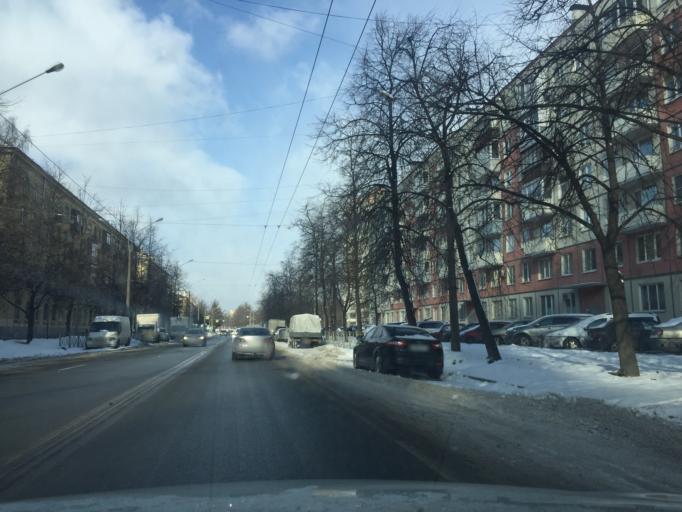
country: RU
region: Leningrad
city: Kalininskiy
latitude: 59.9574
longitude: 30.4223
